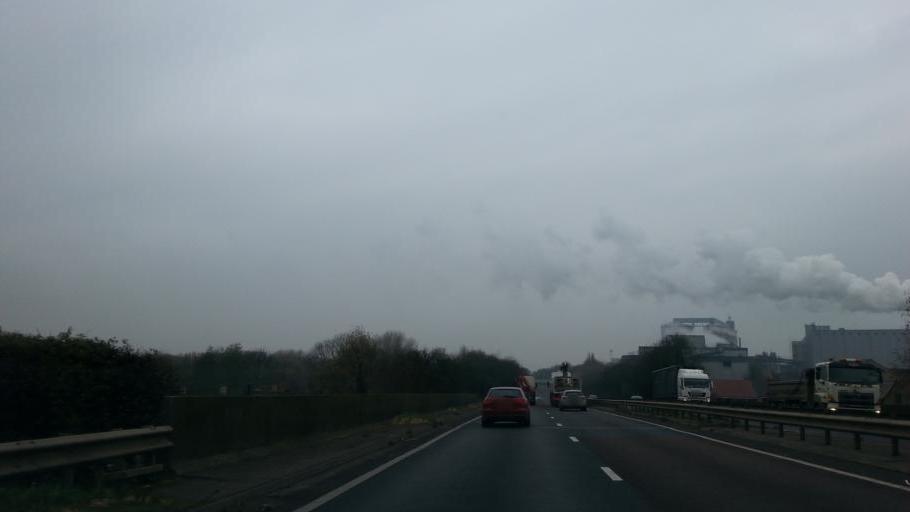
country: GB
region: England
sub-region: Suffolk
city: Bury St Edmunds
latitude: 52.2477
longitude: 0.7241
